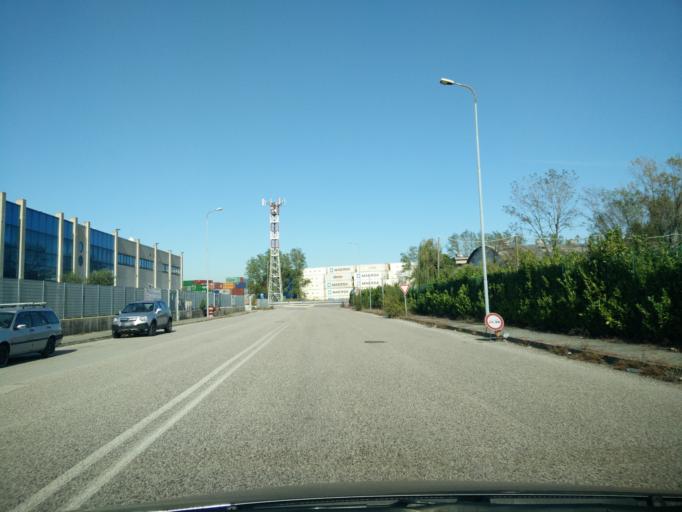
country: IT
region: Veneto
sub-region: Provincia di Venezia
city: Mestre
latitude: 45.4424
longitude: 12.2127
